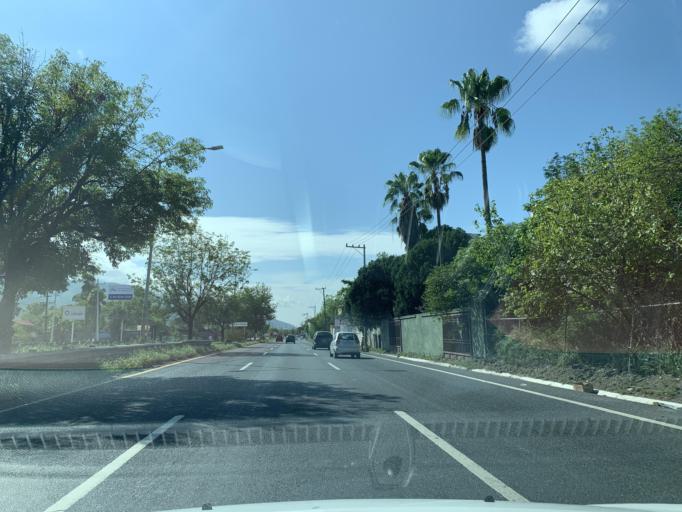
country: MX
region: Nuevo Leon
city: Santiago
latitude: 25.4222
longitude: -100.1462
